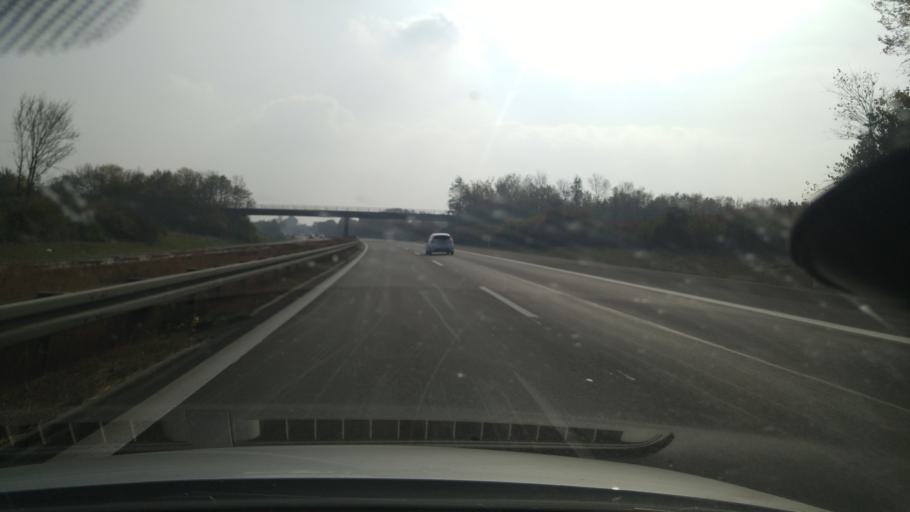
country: DE
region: Baden-Wuerttemberg
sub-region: Karlsruhe Region
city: Empfingen
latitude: 48.4083
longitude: 8.7261
